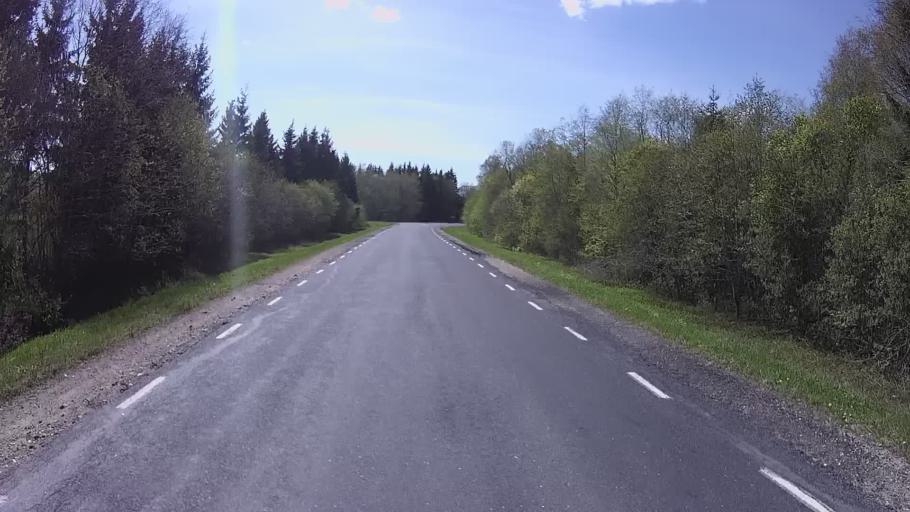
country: EE
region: Laeaene
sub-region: Ridala Parish
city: Uuemoisa
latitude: 59.0084
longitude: 23.7816
